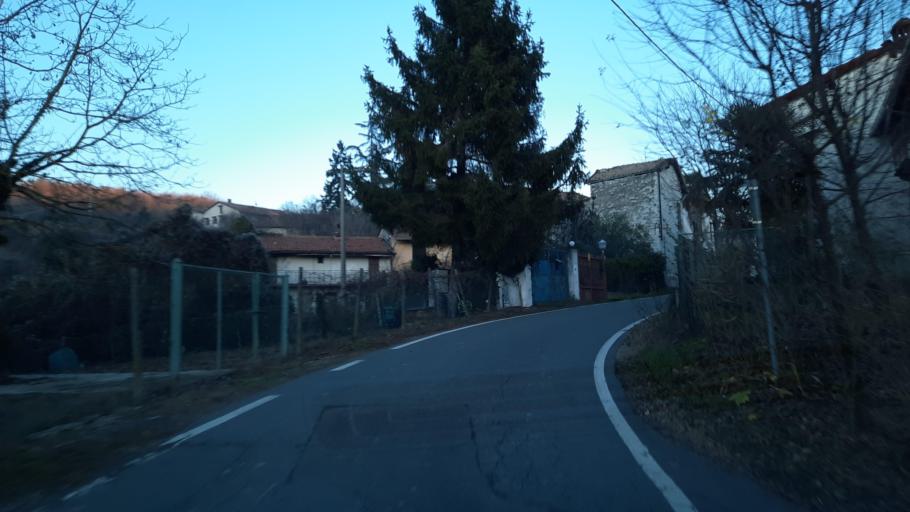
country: IT
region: Piedmont
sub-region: Provincia di Alessandria
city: Mombello Monferrato
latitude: 45.1565
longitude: 8.2591
